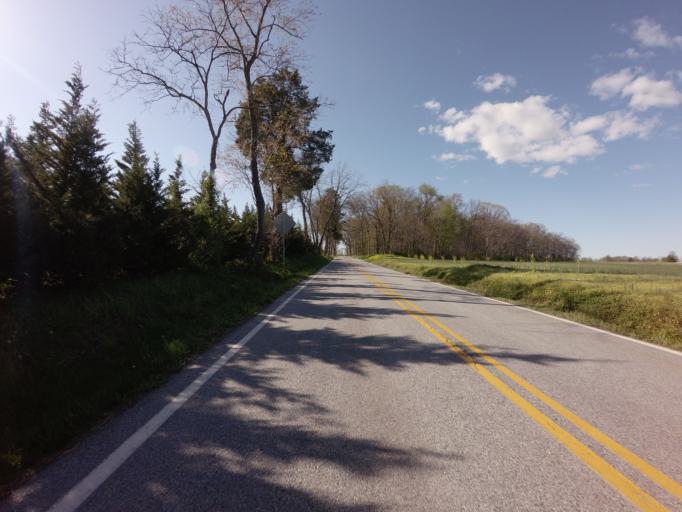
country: US
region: Maryland
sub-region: Frederick County
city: Emmitsburg
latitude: 39.6346
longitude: -77.2865
